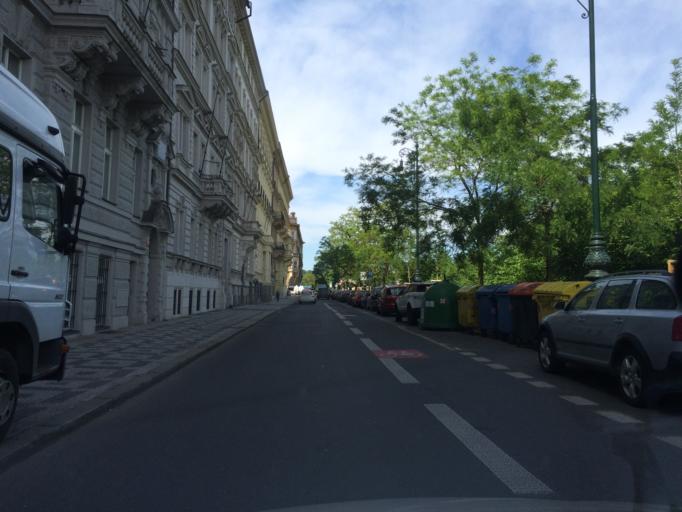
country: CZ
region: Praha
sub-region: Praha 1
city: Mala Strana
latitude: 50.0798
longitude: 14.4081
